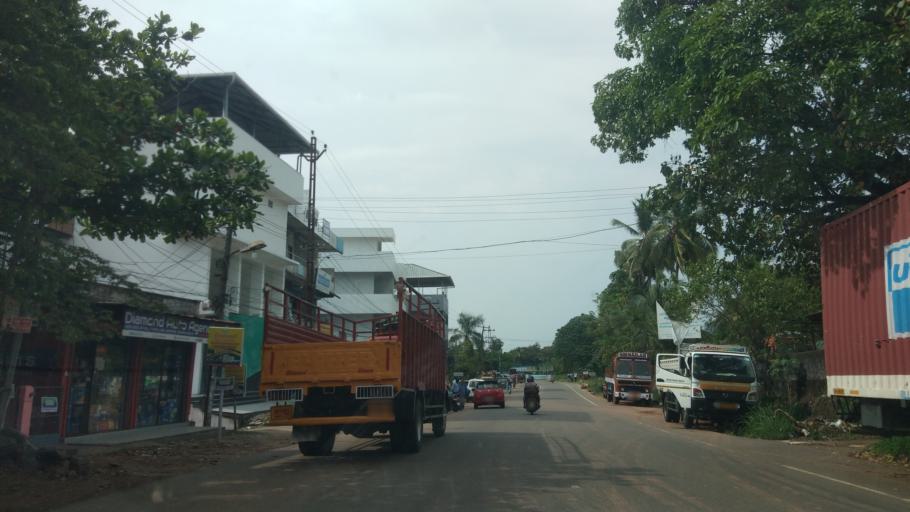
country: IN
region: Kerala
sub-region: Ernakulam
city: Elur
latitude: 10.0646
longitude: 76.3222
